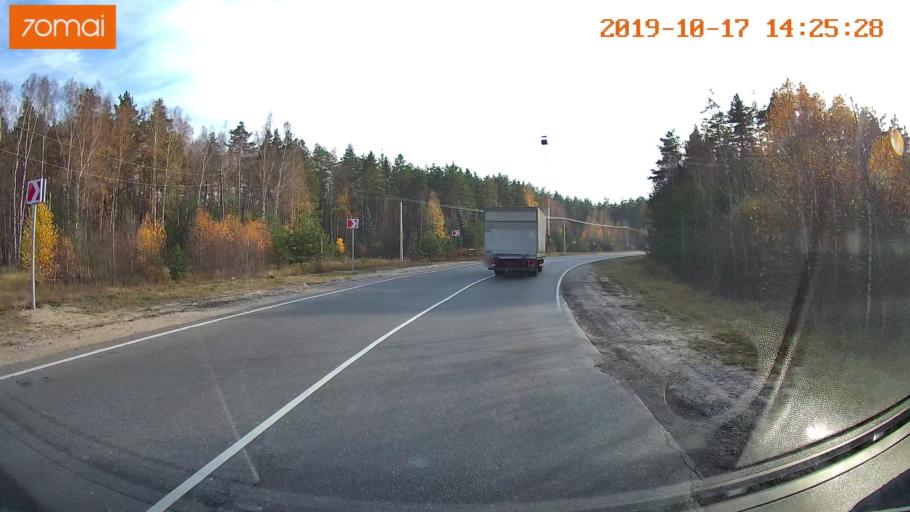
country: RU
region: Moskovskaya
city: Radovitskiy
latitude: 55.0002
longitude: 39.9772
